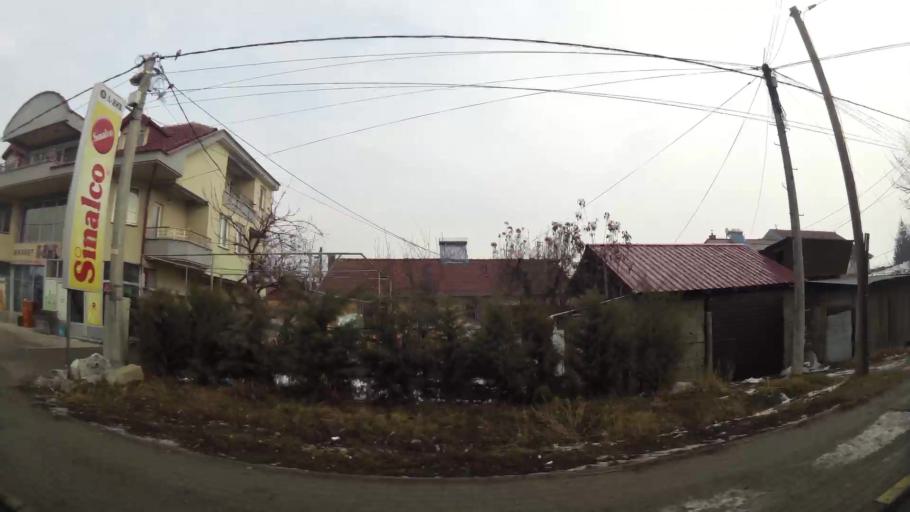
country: MK
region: Ilinden
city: Jurumleri
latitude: 41.9802
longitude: 21.5282
